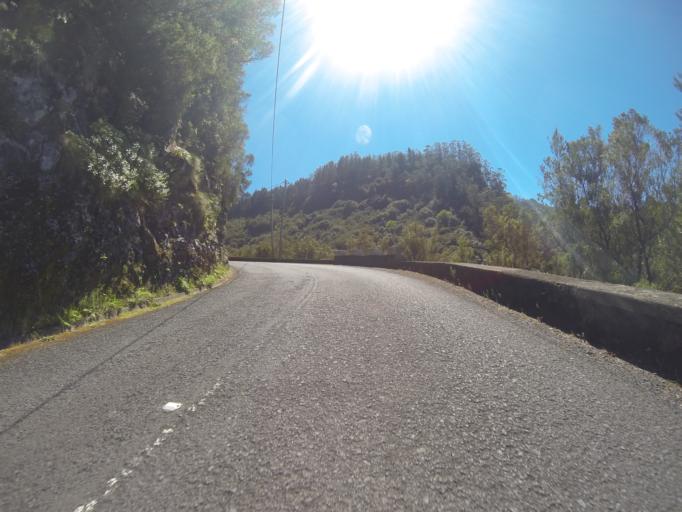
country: PT
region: Madeira
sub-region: Funchal
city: Nossa Senhora do Monte
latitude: 32.7249
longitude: -16.8889
